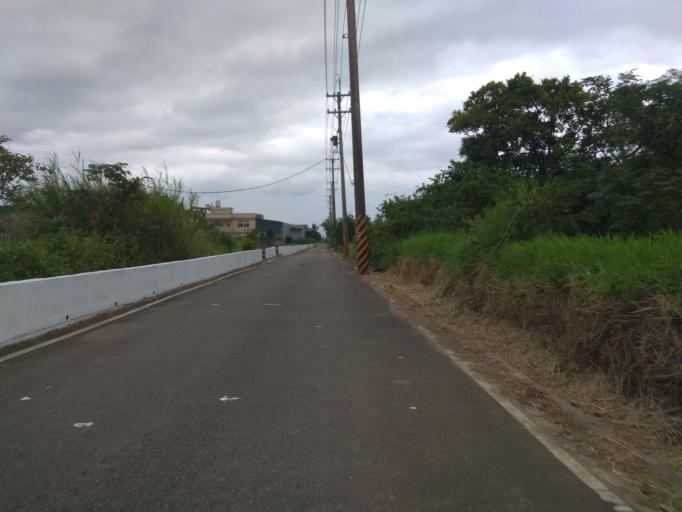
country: TW
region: Taiwan
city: Taoyuan City
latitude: 25.0416
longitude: 121.2207
